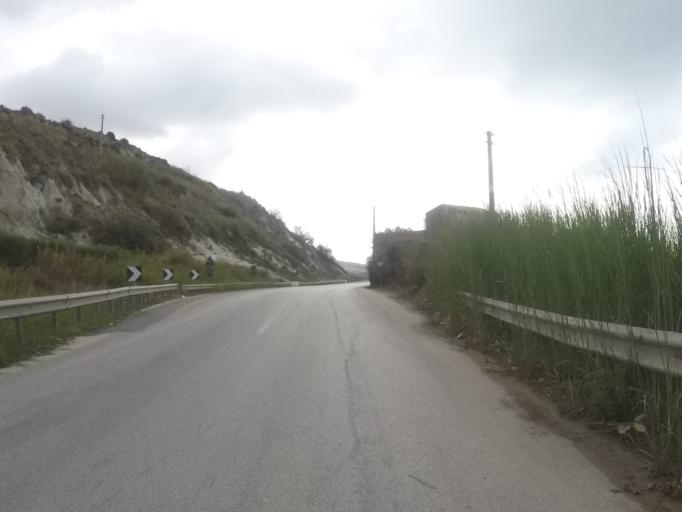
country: IT
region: Sicily
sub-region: Agrigento
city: Porto Empedocle
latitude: 37.2901
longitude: 13.4883
